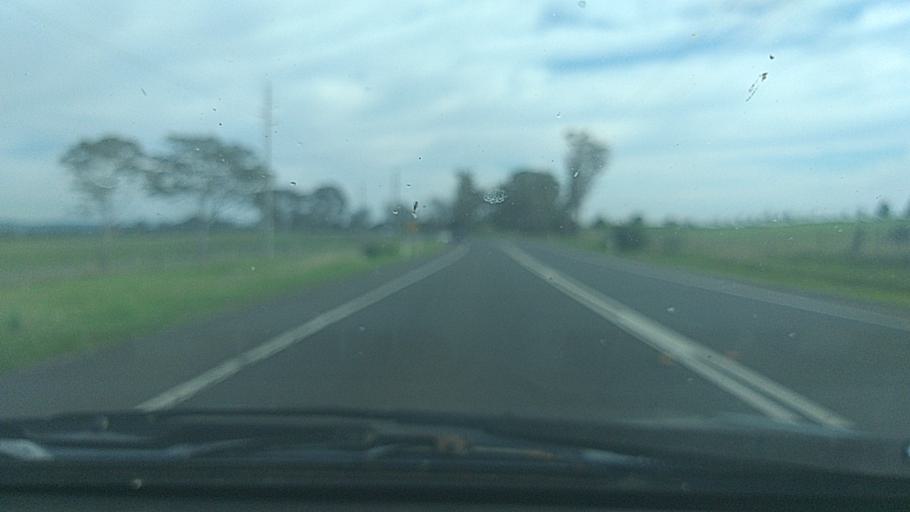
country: AU
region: New South Wales
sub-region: Liverpool
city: Luddenham
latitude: -33.8538
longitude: 150.6932
